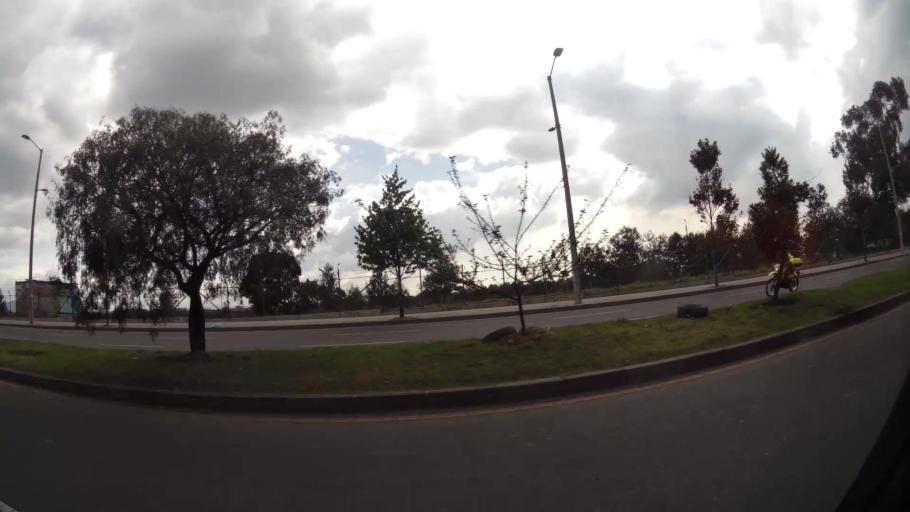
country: CO
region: Cundinamarca
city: Cota
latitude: 4.7224
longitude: -74.0974
